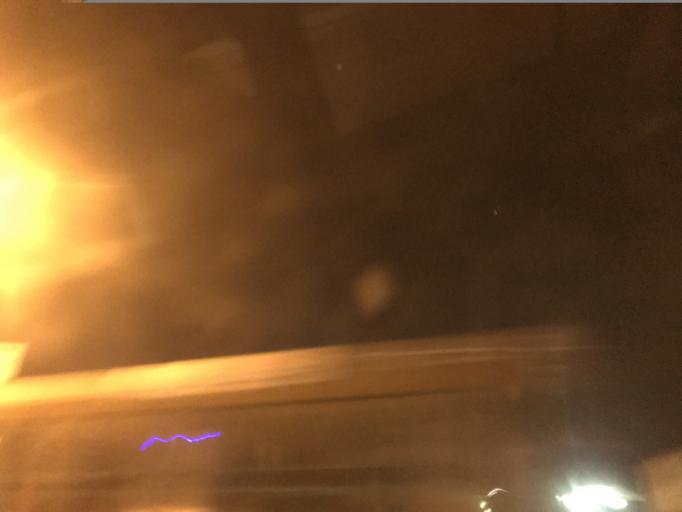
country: TR
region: Istanbul
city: Pendik
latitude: 40.8968
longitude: 29.2544
